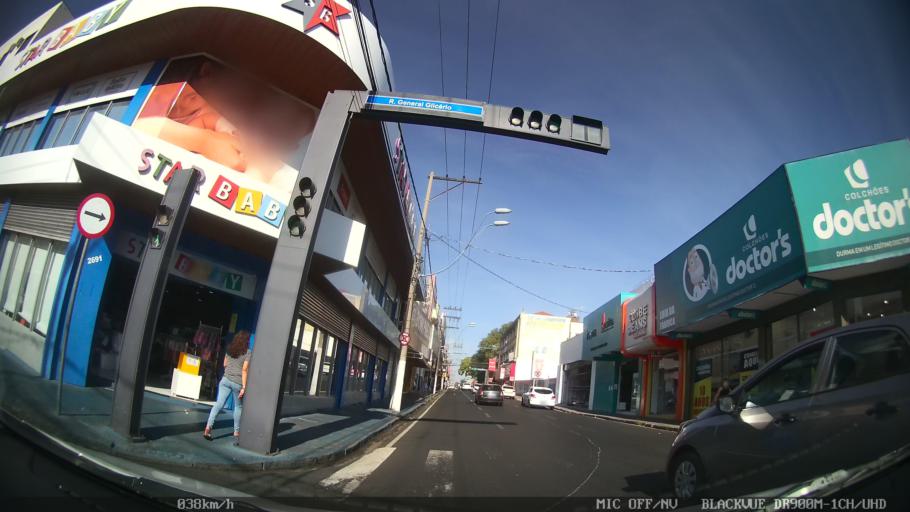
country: BR
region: Sao Paulo
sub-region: Sao Jose Do Rio Preto
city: Sao Jose do Rio Preto
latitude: -20.8091
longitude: -49.3791
